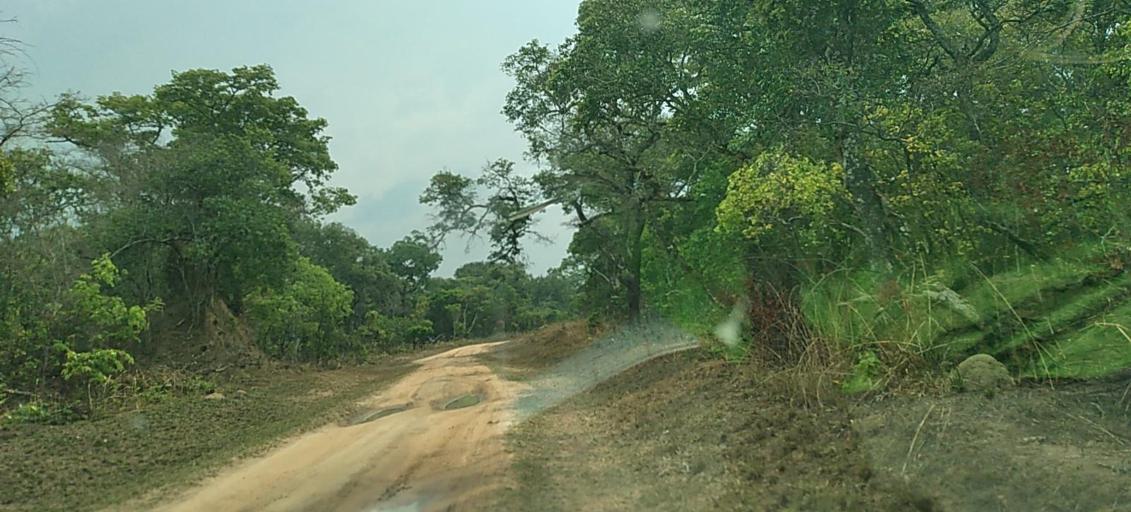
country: ZM
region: North-Western
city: Mwinilunga
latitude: -11.4691
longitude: 24.4656
